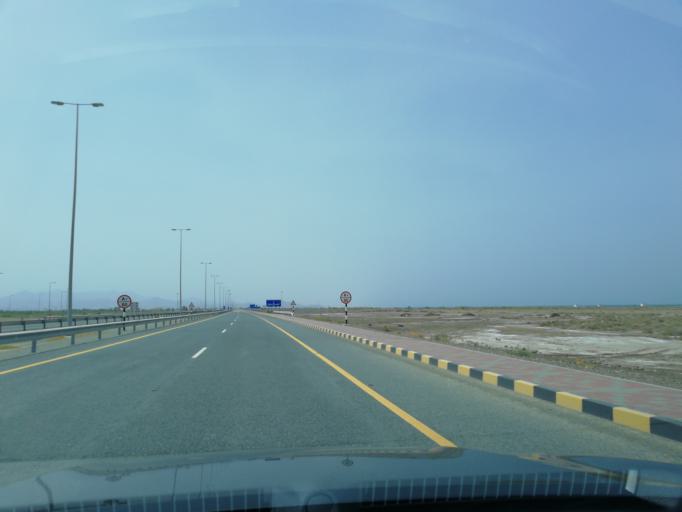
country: OM
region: Al Batinah
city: Shinas
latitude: 24.8590
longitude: 56.4163
